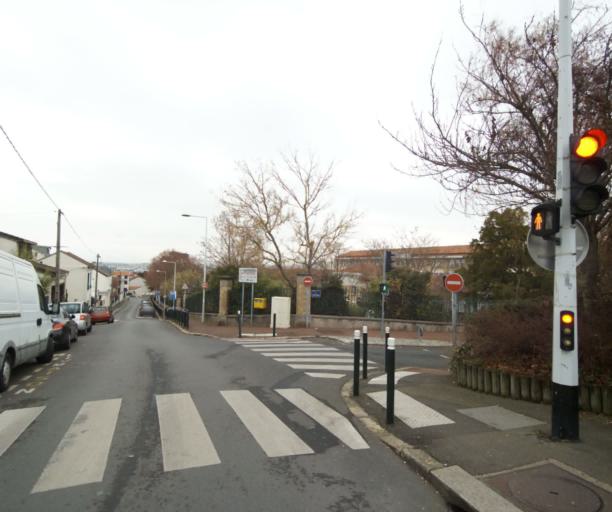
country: FR
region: Ile-de-France
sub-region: Departement des Hauts-de-Seine
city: Nanterre
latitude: 48.8816
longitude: 2.2022
